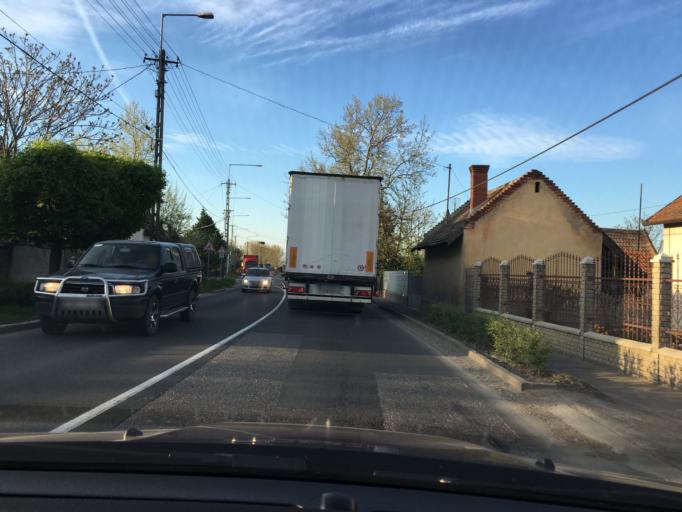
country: HU
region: Hajdu-Bihar
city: Mikepercs
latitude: 47.4469
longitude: 21.6324
